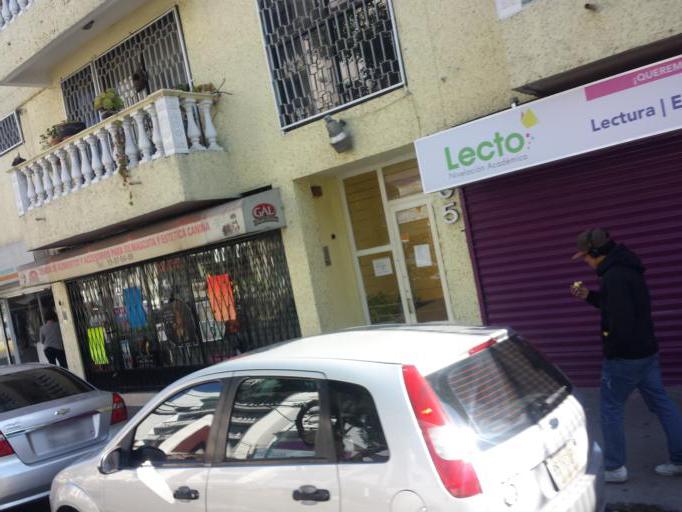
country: MX
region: Mexico
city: Colonia Lindavista
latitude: 19.5003
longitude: -99.1303
